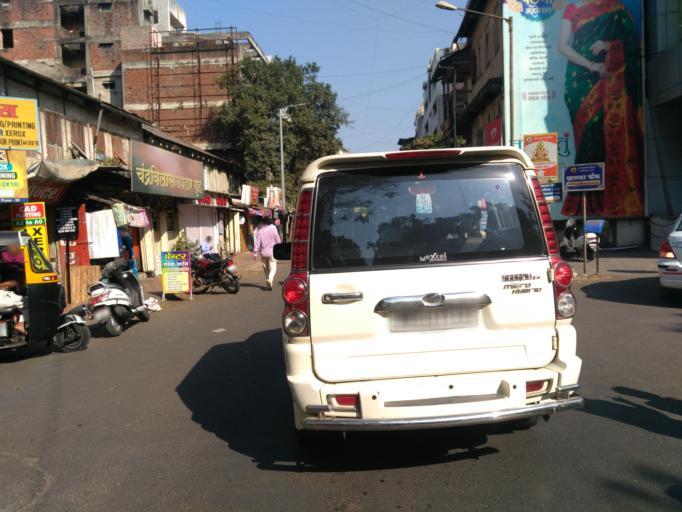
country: IN
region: Maharashtra
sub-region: Pune Division
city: Pune
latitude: 18.5132
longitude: 73.8473
